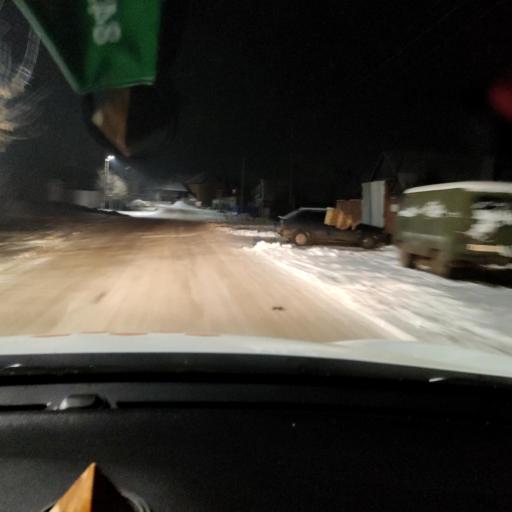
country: RU
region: Tatarstan
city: Stolbishchi
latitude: 55.6515
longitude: 49.2109
